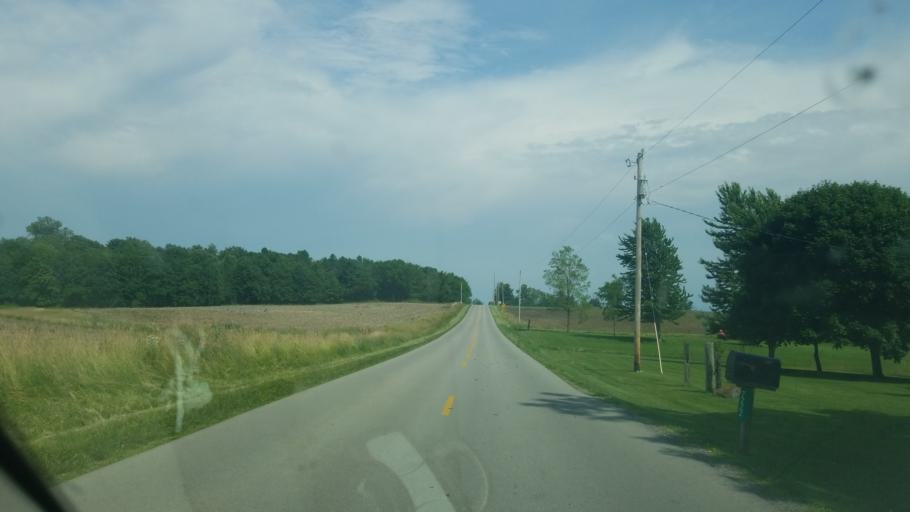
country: US
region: Ohio
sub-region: Champaign County
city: North Lewisburg
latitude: 40.2969
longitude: -83.6453
